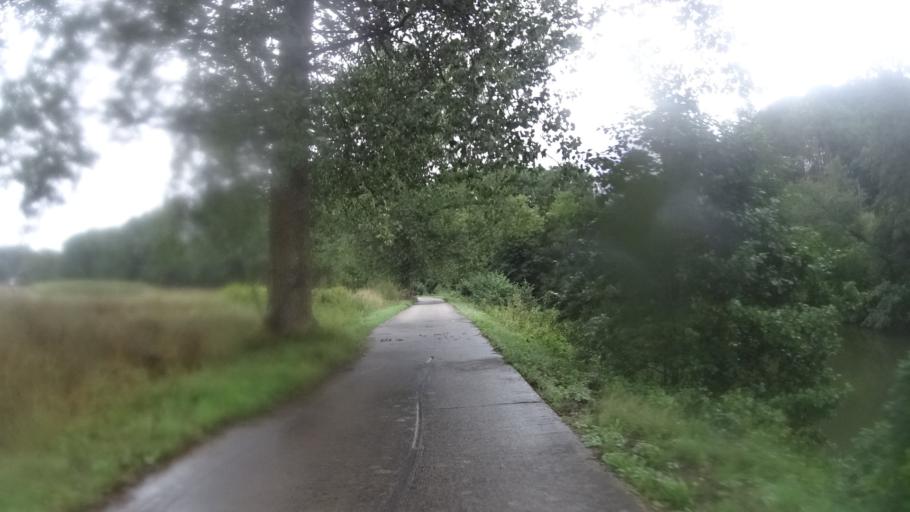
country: BE
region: Wallonia
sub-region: Province du Hainaut
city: Lobbes
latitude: 50.3429
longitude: 4.2485
